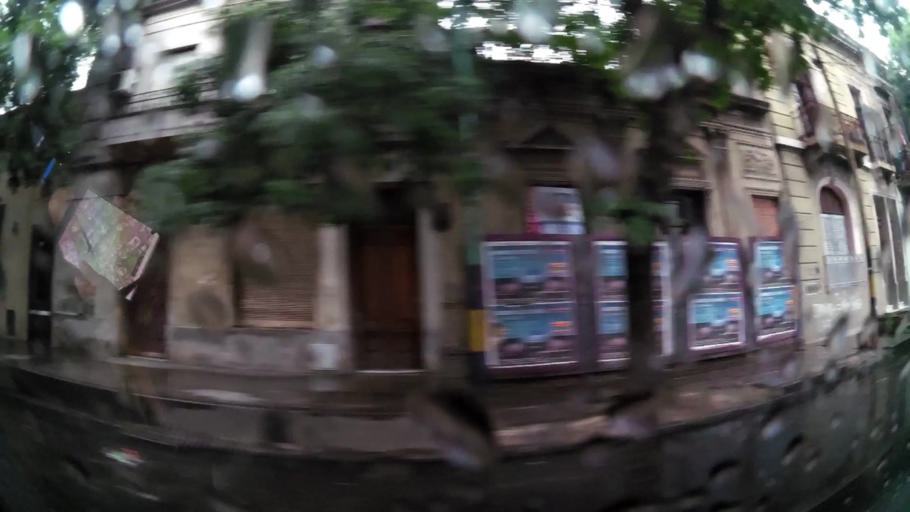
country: AR
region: Buenos Aires
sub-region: Partido de Avellaneda
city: Avellaneda
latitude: -34.6375
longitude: -58.3666
